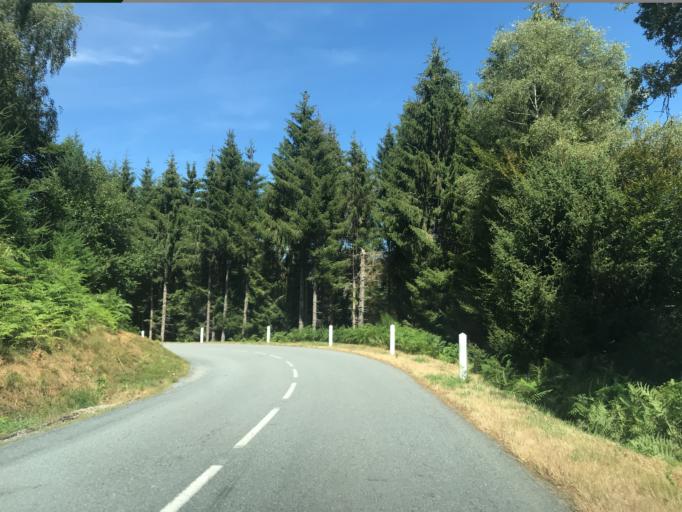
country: FR
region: Limousin
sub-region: Departement de la Creuse
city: Felletin
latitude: 45.7787
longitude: 2.1388
